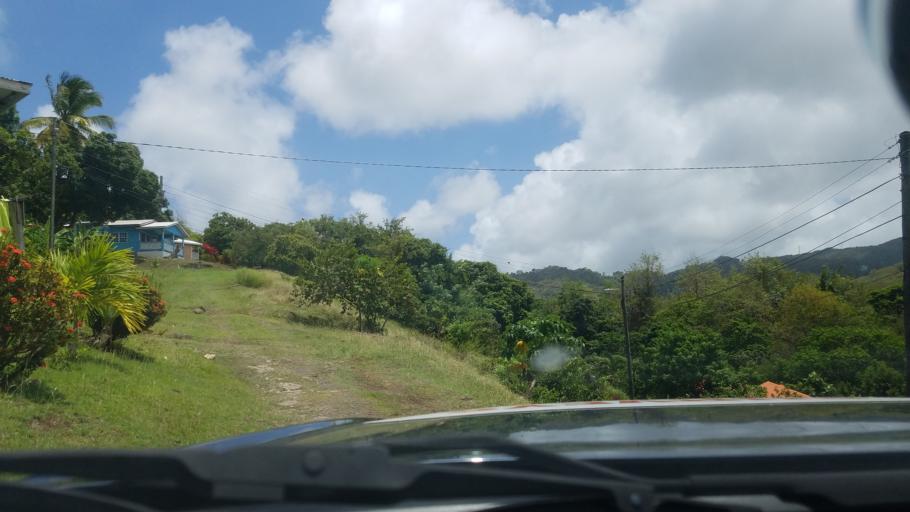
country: LC
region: Gros-Islet
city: Gros Islet
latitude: 14.0533
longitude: -60.9279
